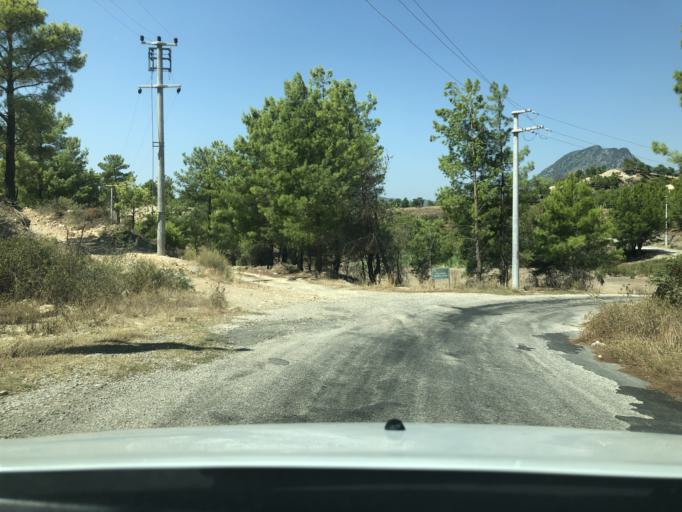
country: TR
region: Antalya
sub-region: Manavgat
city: Kizilagac
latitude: 36.8649
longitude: 31.5592
